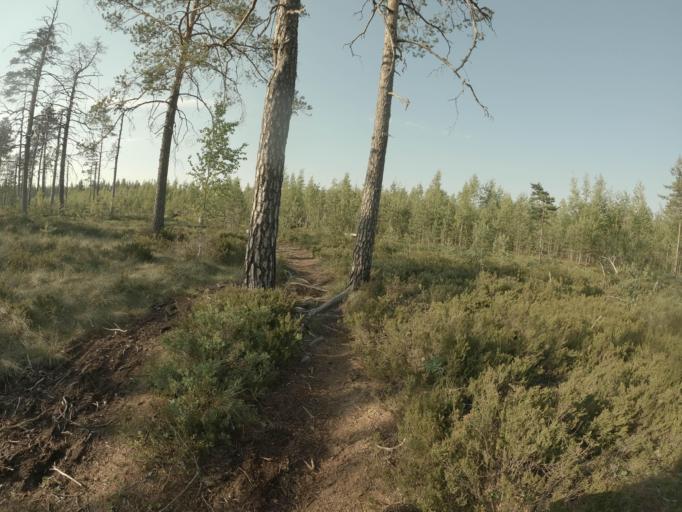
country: RU
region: Leningrad
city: Yakovlevo
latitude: 60.4417
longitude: 29.2402
